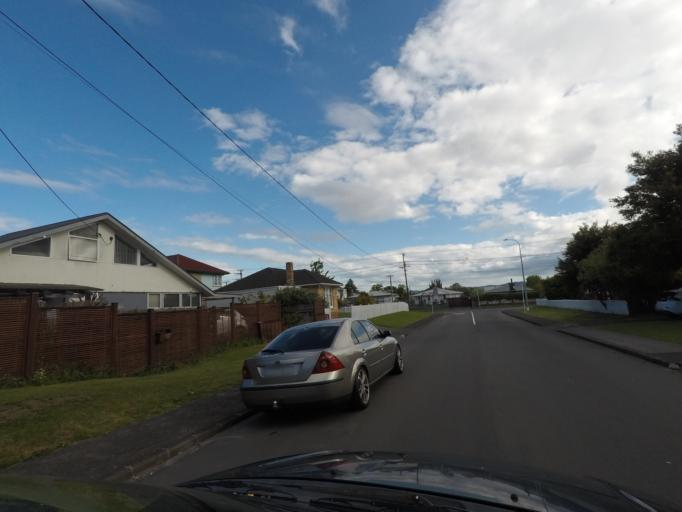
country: NZ
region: Auckland
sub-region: Auckland
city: Rosebank
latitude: -36.8683
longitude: 174.6422
